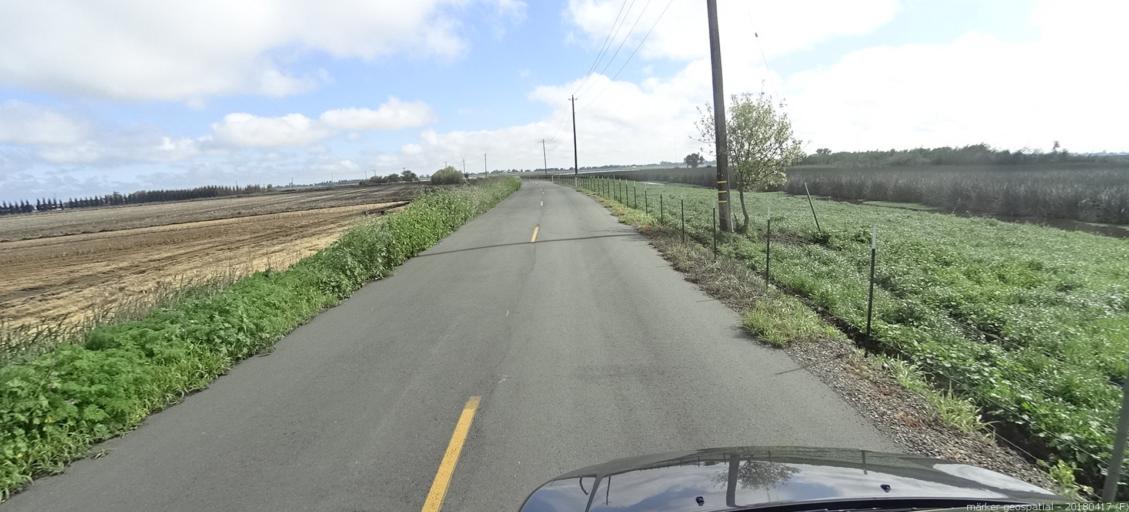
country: US
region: California
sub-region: Sacramento County
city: Walnut Grove
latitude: 38.2469
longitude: -121.5616
